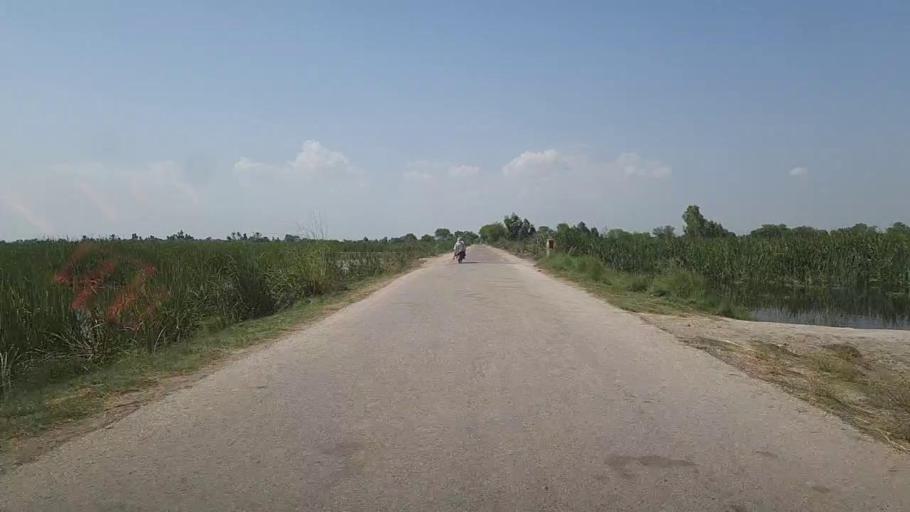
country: PK
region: Sindh
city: Khairpur
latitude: 28.0717
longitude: 69.6411
